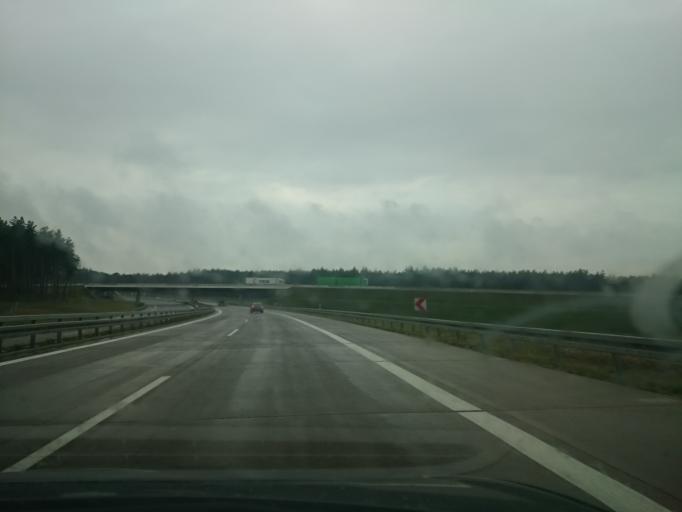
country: DE
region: Brandenburg
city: Kremmen
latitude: 52.7108
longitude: 13.0163
